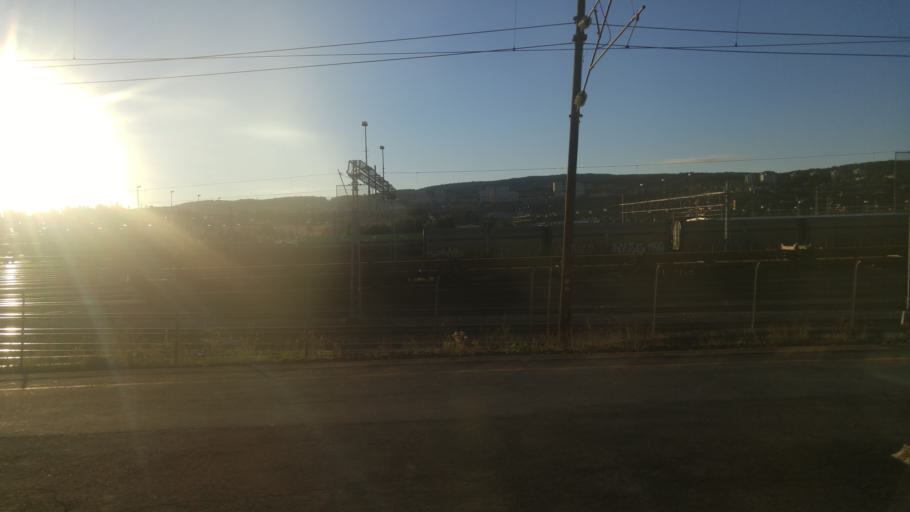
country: NO
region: Oslo
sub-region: Oslo
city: Oslo
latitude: 59.9328
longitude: 10.8354
